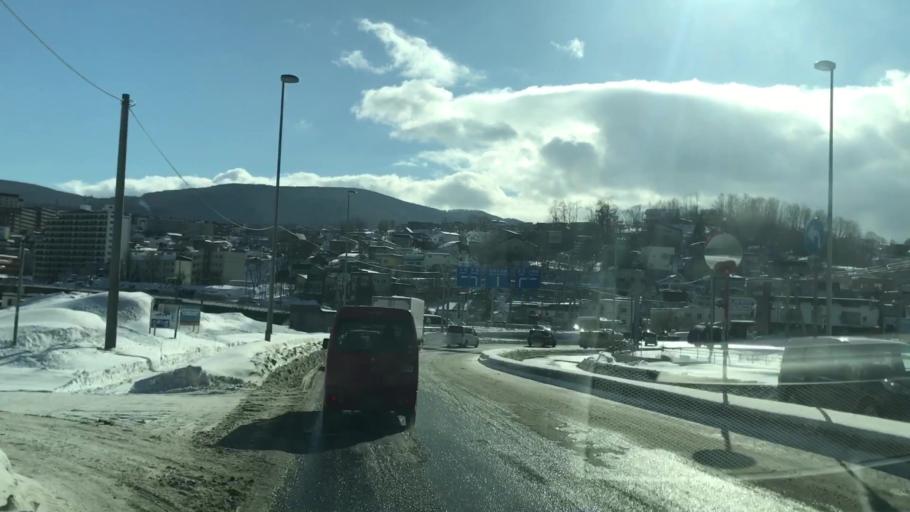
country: JP
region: Hokkaido
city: Otaru
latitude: 43.1795
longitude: 141.0377
